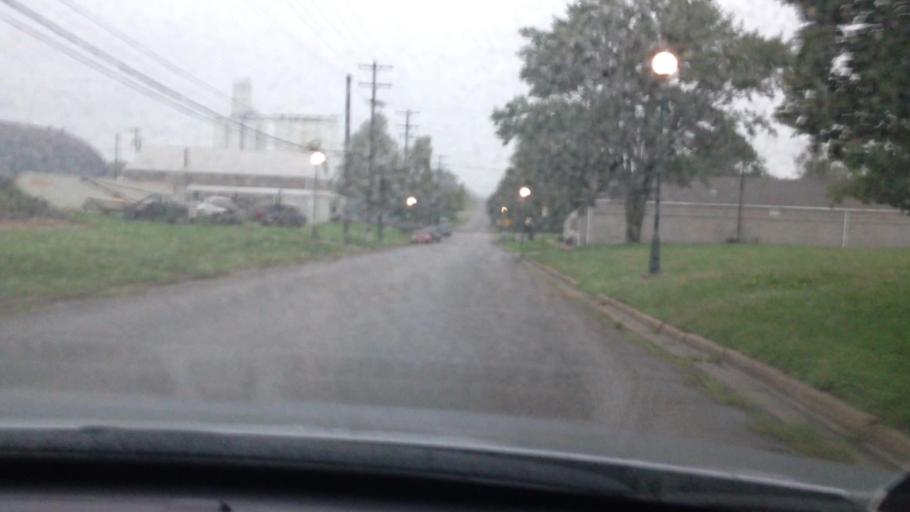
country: US
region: Kansas
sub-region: Brown County
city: Hiawatha
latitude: 39.8503
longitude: -95.5459
